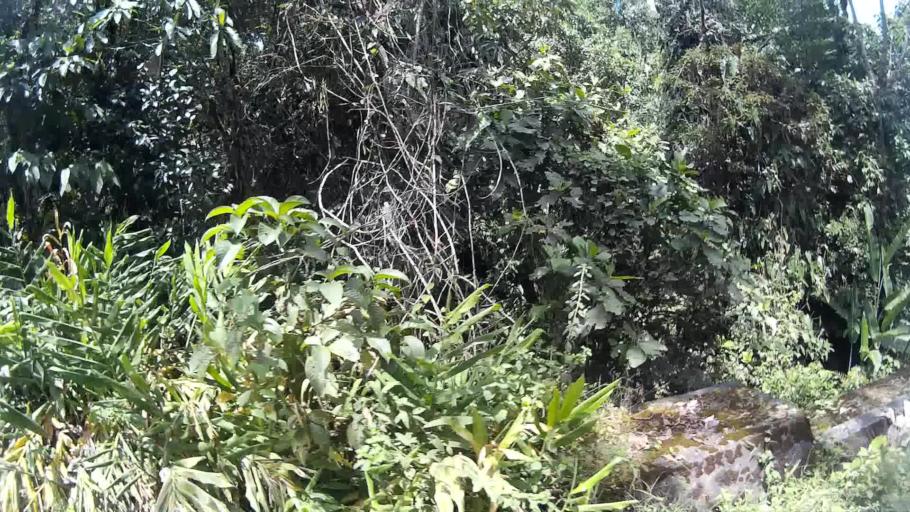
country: CO
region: Quindio
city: Filandia
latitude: 4.7130
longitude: -75.6621
